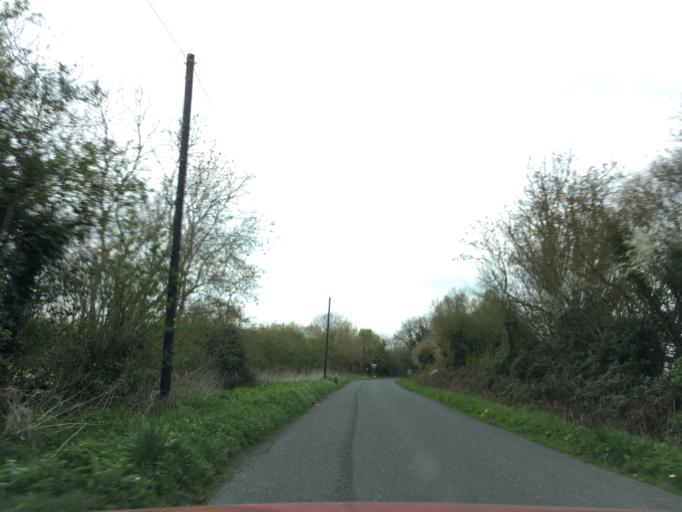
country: GB
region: England
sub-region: Oxfordshire
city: Bicester
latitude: 51.8818
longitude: -1.1697
